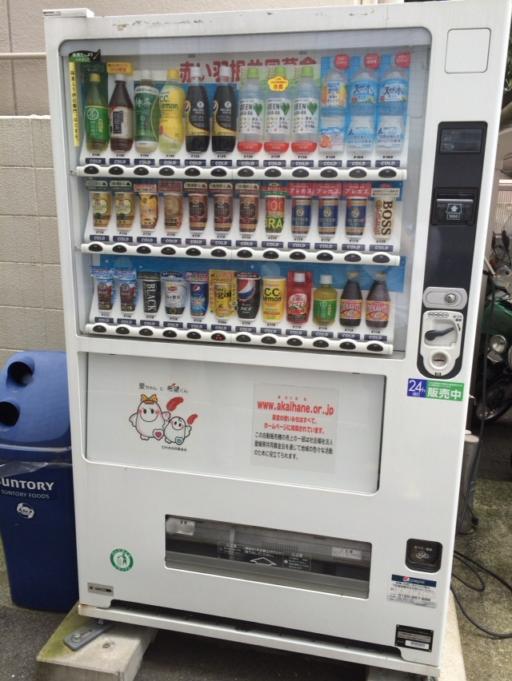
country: JP
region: Ehime
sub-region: Shikoku-chuo Shi
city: Matsuyama
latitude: 33.8469
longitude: 132.7751
